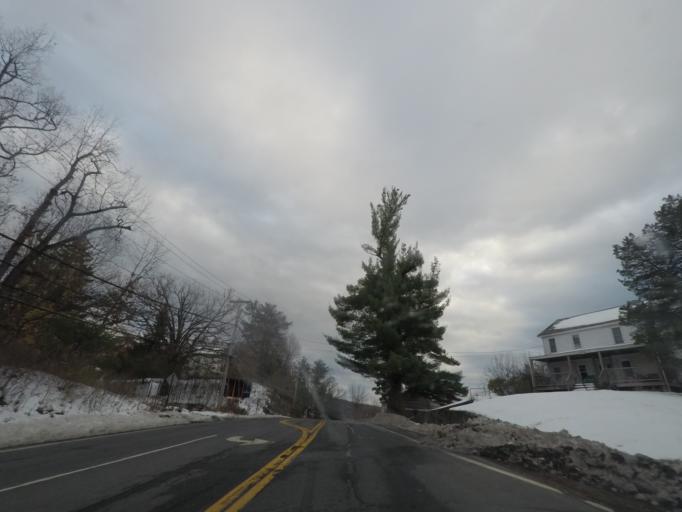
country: US
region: New York
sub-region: Ulster County
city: Kingston
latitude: 41.9186
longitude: -74.0155
